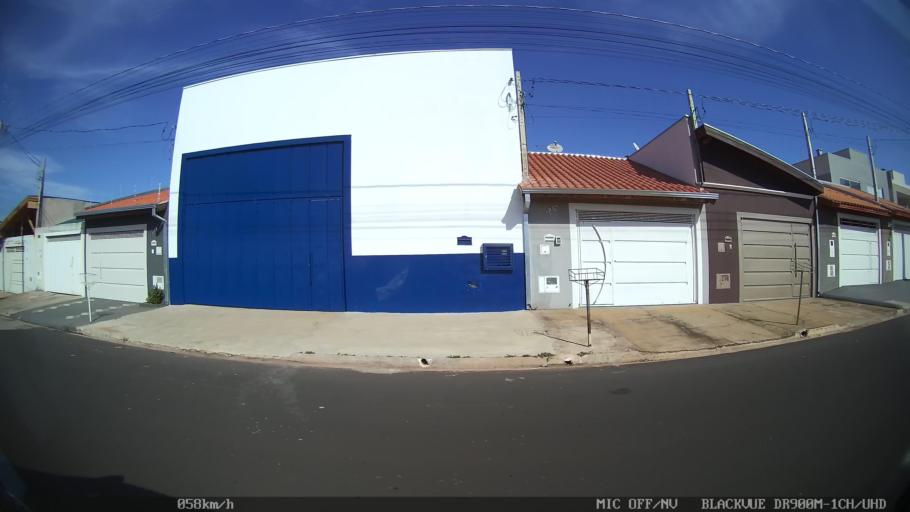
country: BR
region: Sao Paulo
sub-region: Franca
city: Franca
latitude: -20.5063
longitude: -47.4352
